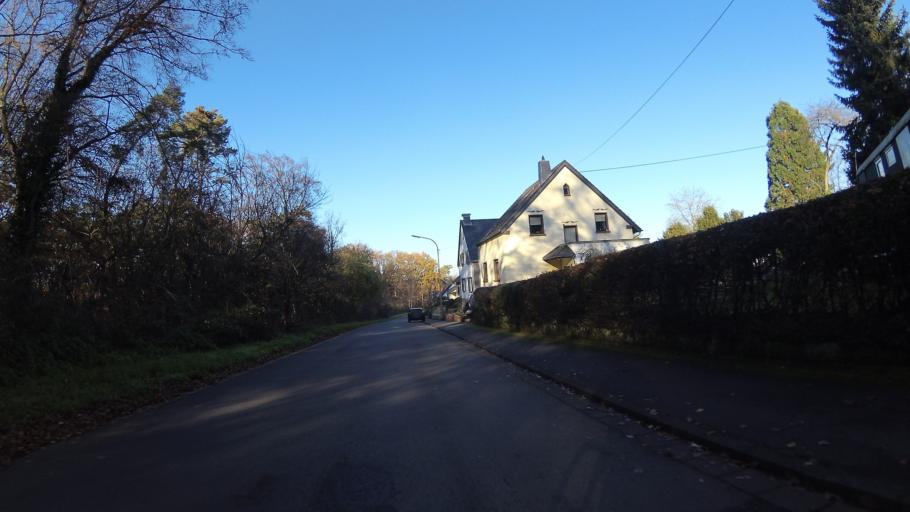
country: DE
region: Saarland
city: Schwalbach
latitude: 49.2945
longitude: 6.8130
